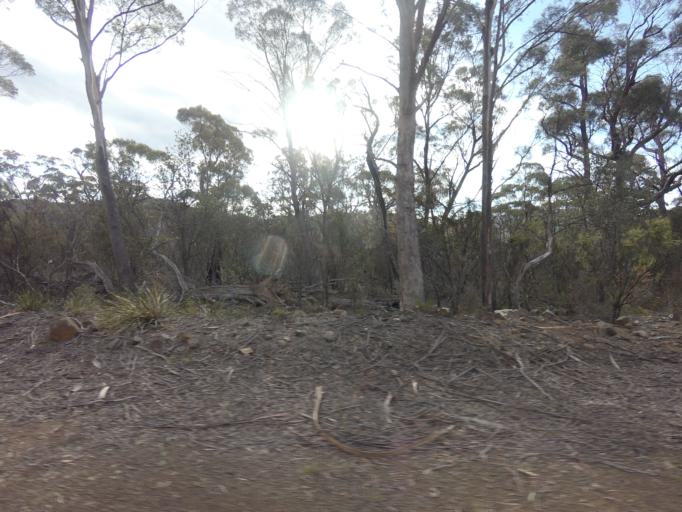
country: AU
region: Tasmania
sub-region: Break O'Day
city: St Helens
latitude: -41.8604
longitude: 148.0237
